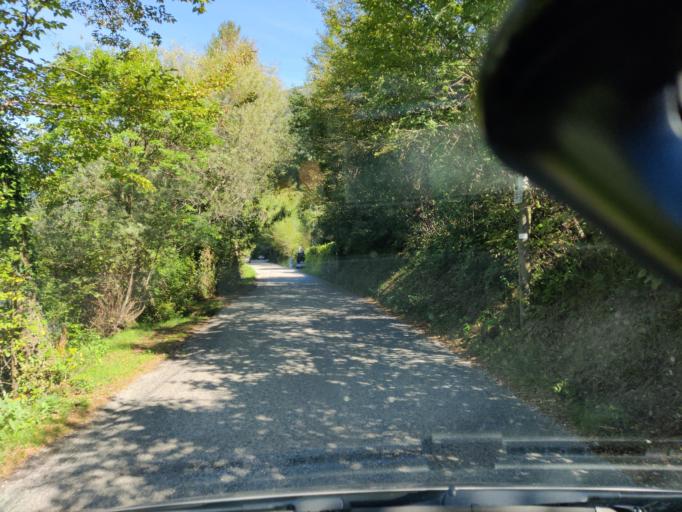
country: IT
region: Lombardy
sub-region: Provincia di Brescia
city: Anfo
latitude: 45.7703
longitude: 10.5202
